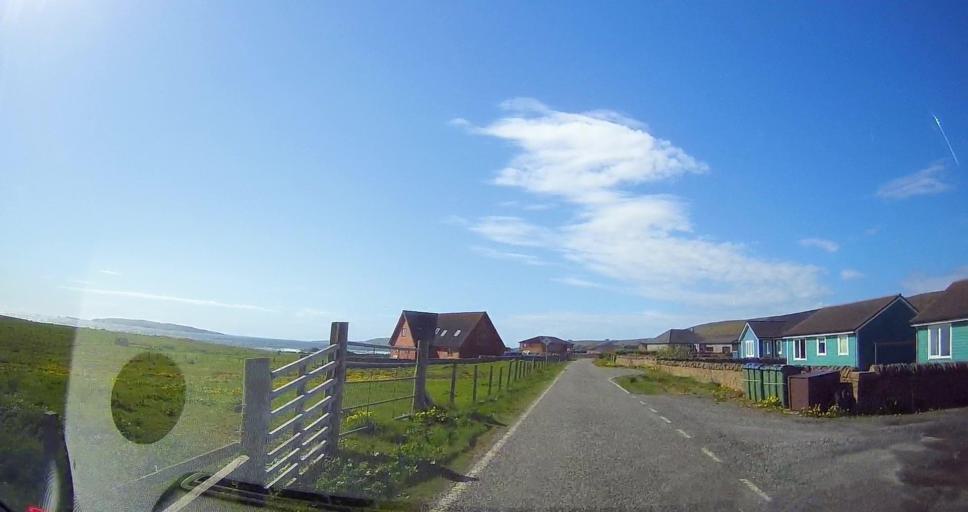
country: GB
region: Scotland
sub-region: Shetland Islands
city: Sandwick
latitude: 60.0370
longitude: -1.2182
